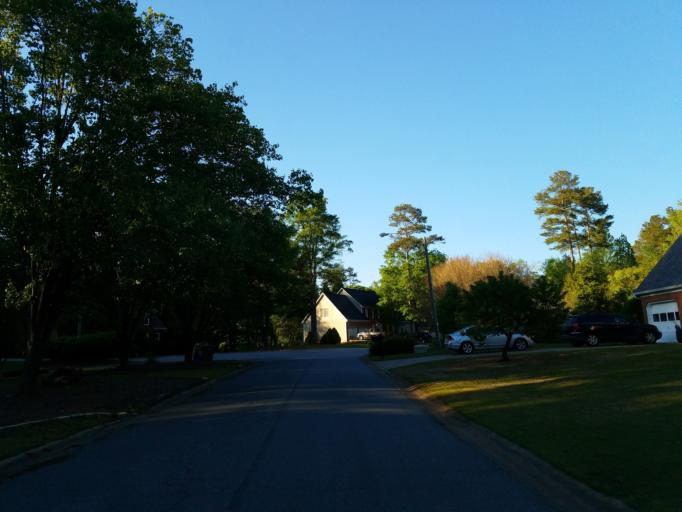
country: US
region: Georgia
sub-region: Cobb County
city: Powder Springs
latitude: 33.9204
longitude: -84.6432
